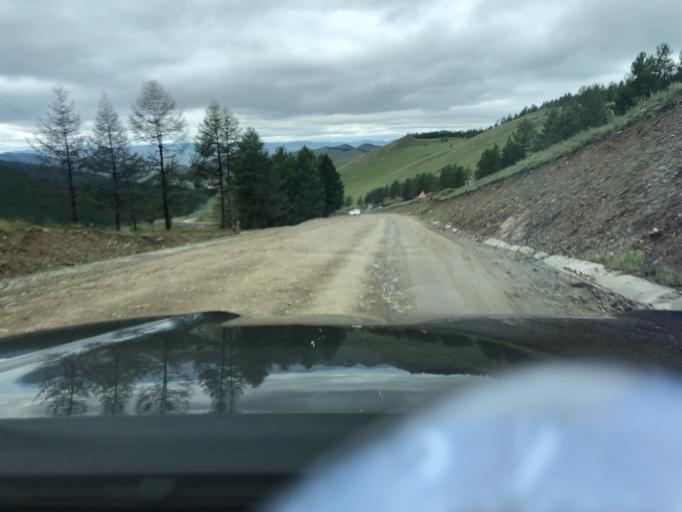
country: MN
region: Ulaanbaatar
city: Ulaanbaatar
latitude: 48.0810
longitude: 106.8398
